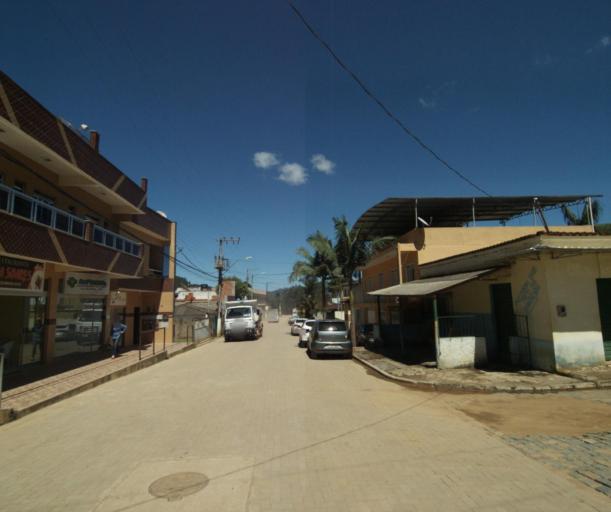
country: BR
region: Minas Gerais
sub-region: Espera Feliz
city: Espera Feliz
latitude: -20.5545
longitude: -41.8182
